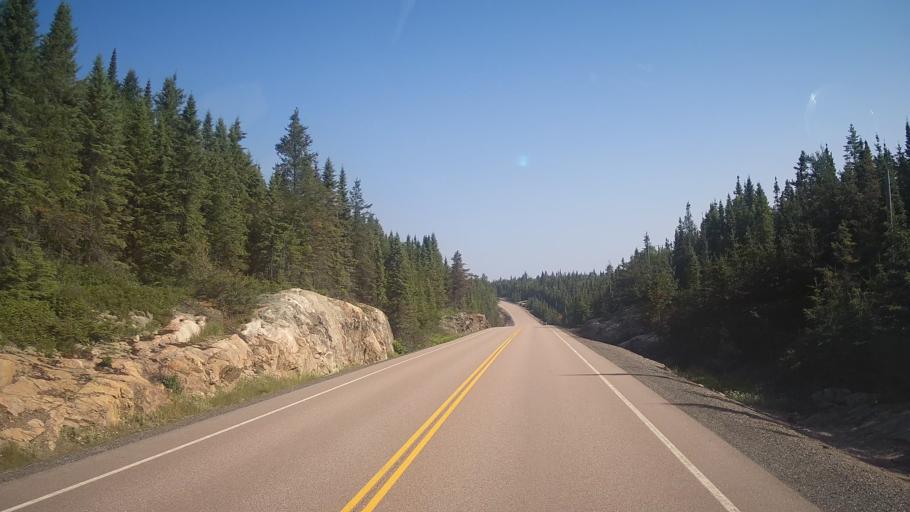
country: CA
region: Ontario
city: Rayside-Balfour
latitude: 47.0343
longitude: -81.6368
